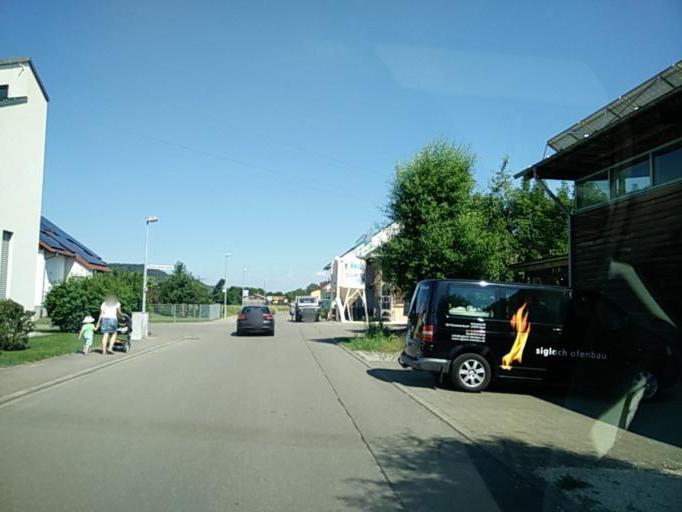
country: DE
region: Baden-Wuerttemberg
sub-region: Tuebingen Region
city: Rottenburg
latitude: 48.5244
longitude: 8.9696
